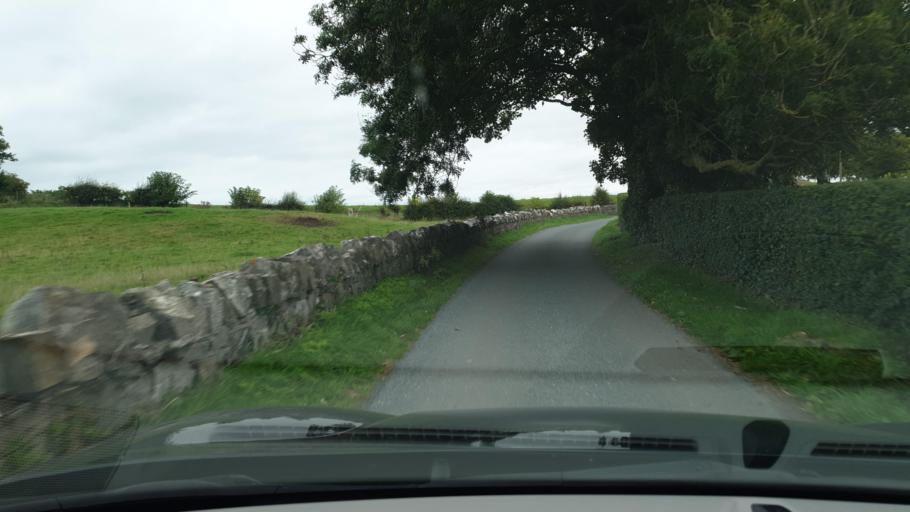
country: IE
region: Leinster
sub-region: An Mhi
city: Dunshaughlin
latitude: 53.4921
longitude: -6.5710
